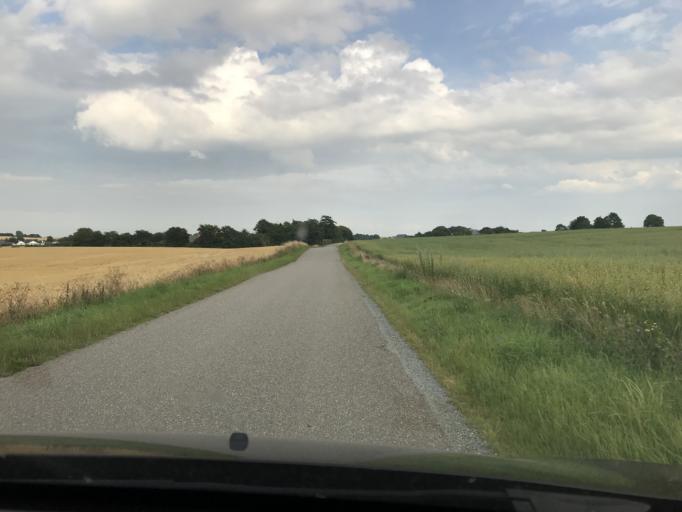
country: DK
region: South Denmark
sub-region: Vejle Kommune
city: Jelling
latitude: 55.8027
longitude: 9.4483
